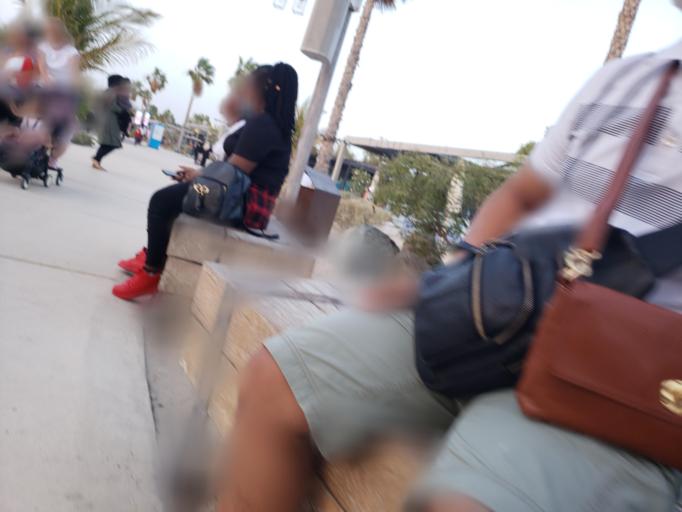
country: AE
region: Dubai
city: Dubai
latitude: 25.2302
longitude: 55.2585
